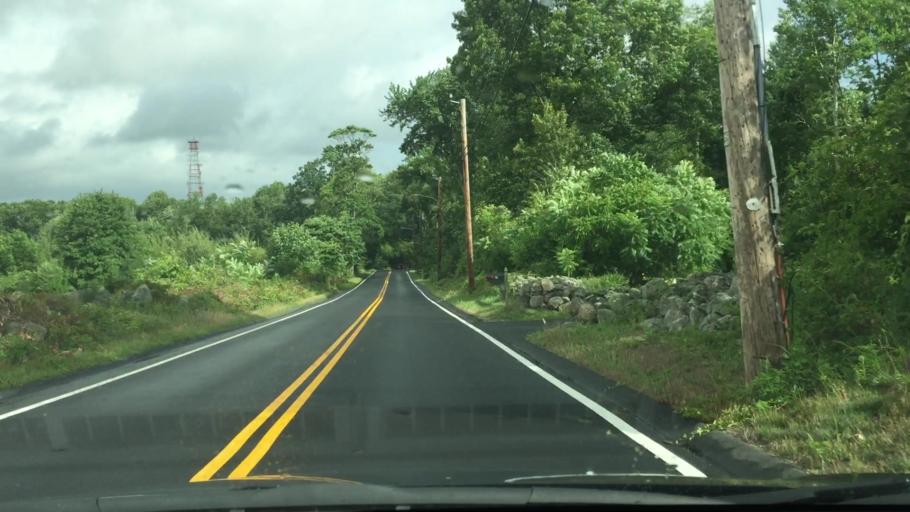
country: US
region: Massachusetts
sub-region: Middlesex County
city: Littleton Common
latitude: 42.5188
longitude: -71.4560
